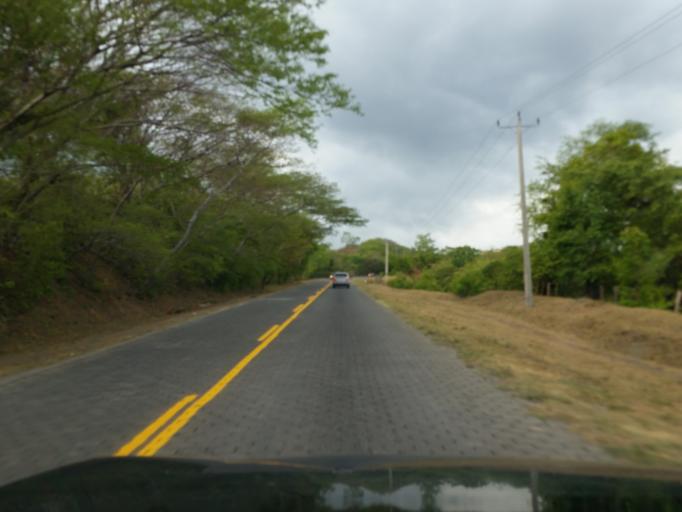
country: NI
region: Managua
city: San Rafael del Sur
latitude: 11.8753
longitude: -86.5152
